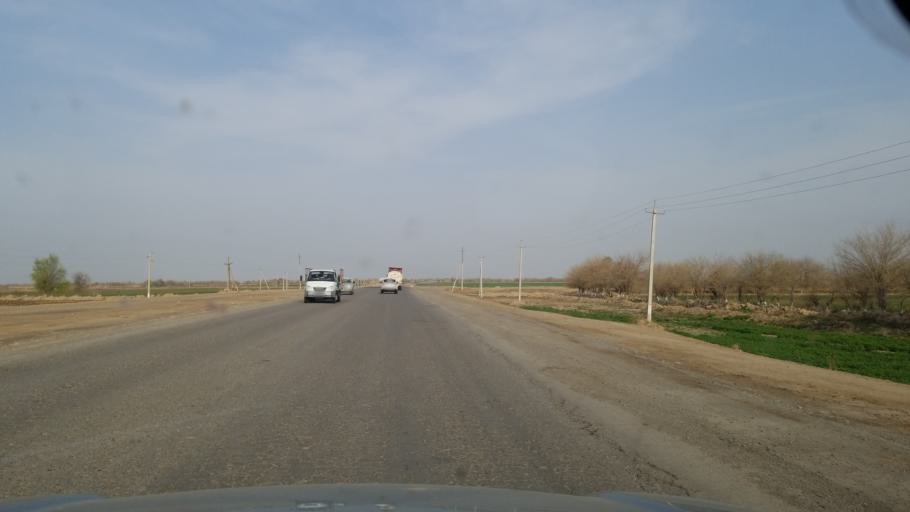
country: TM
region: Mary
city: Bayramaly
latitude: 37.6128
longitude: 62.2867
